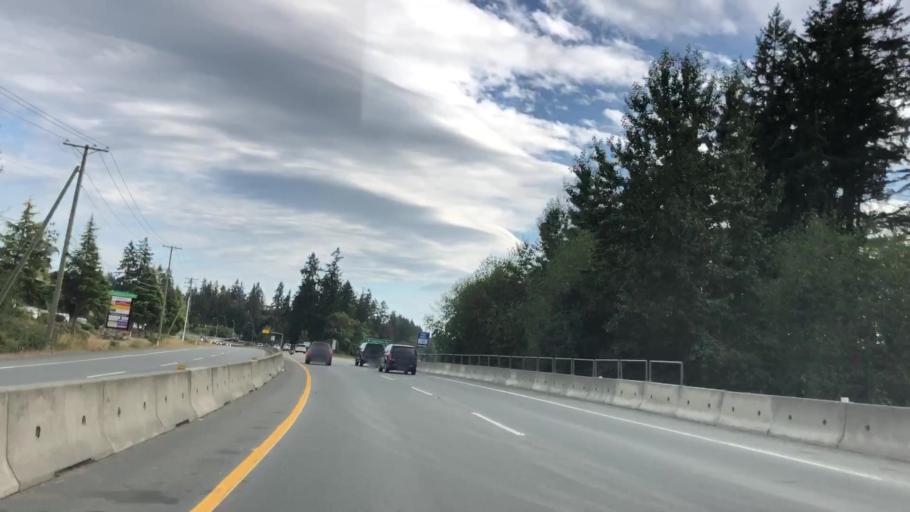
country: CA
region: British Columbia
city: Duncan
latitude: 48.7117
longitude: -123.6100
